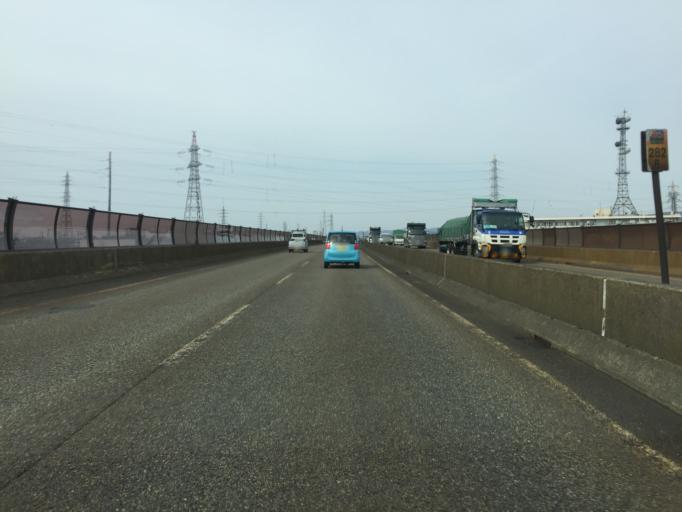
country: JP
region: Niigata
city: Nagaoka
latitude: 37.4414
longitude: 138.8694
